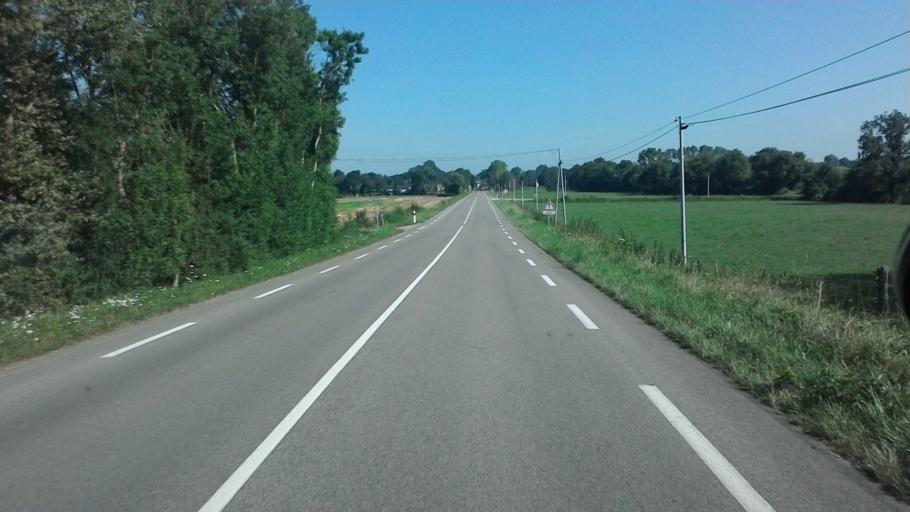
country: FR
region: Rhone-Alpes
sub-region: Departement de l'Ain
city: Montrevel-en-Bresse
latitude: 46.3929
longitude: 5.1149
